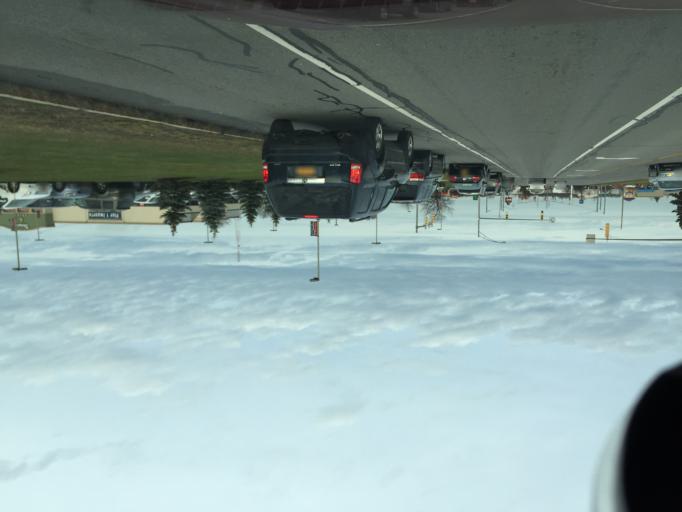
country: US
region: New York
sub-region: Monroe County
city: Rochester
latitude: 43.0846
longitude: -77.6297
